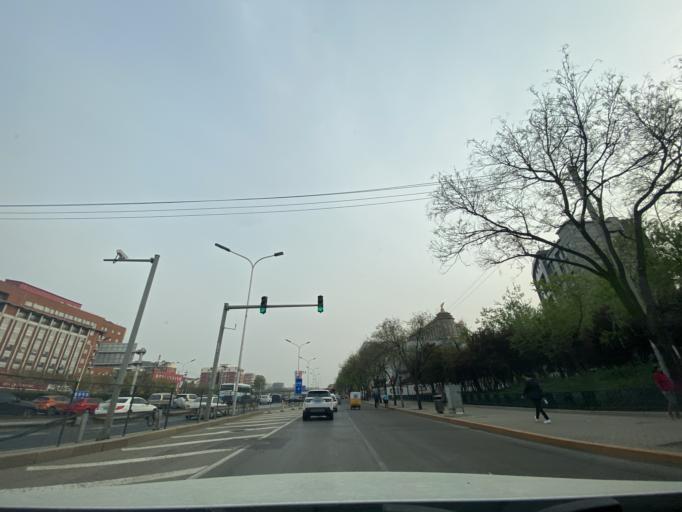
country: CN
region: Beijing
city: Sijiqing
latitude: 39.9375
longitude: 116.2679
